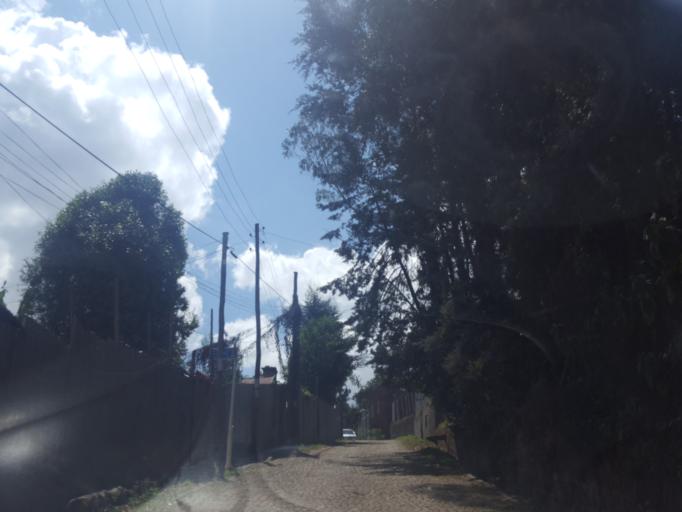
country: ET
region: Adis Abeba
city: Addis Ababa
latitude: 9.0626
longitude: 38.7654
